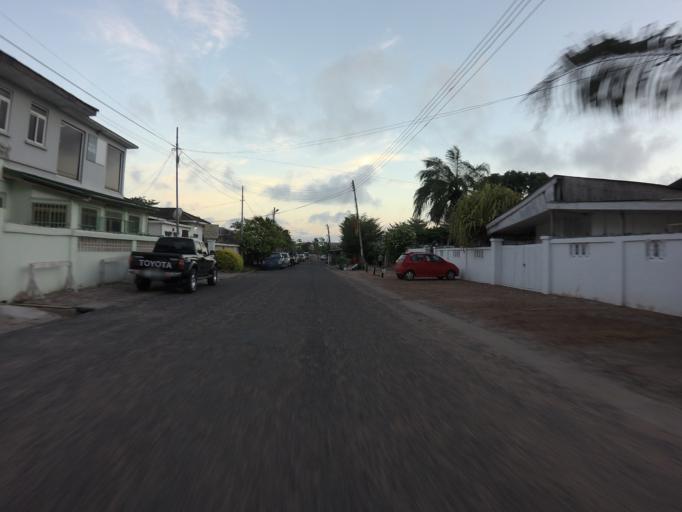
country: GH
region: Greater Accra
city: Accra
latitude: 5.5578
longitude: -0.1725
